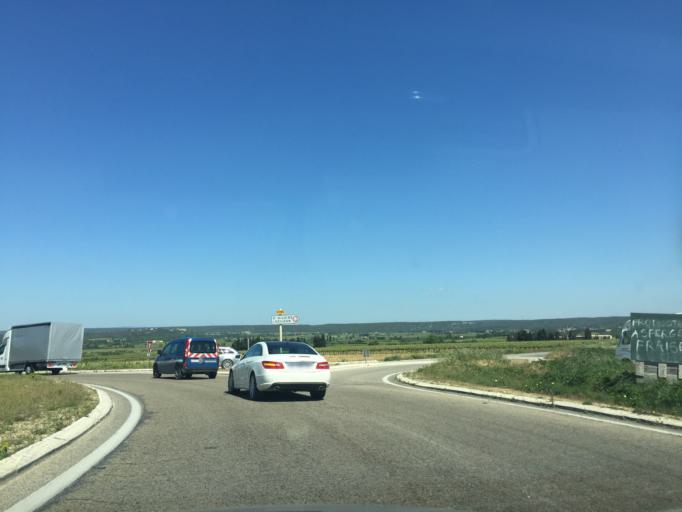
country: FR
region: Languedoc-Roussillon
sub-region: Departement du Gard
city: Remoulins
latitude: 43.9400
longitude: 4.5975
